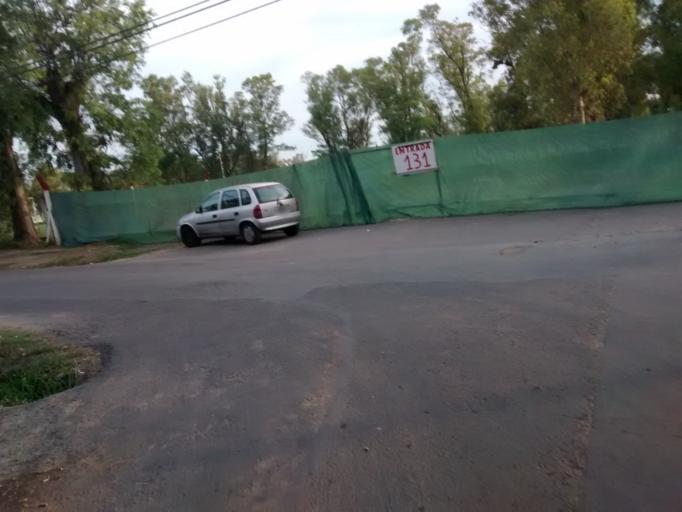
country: AR
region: Buenos Aires
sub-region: Partido de La Plata
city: La Plata
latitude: -34.8856
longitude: -58.0662
